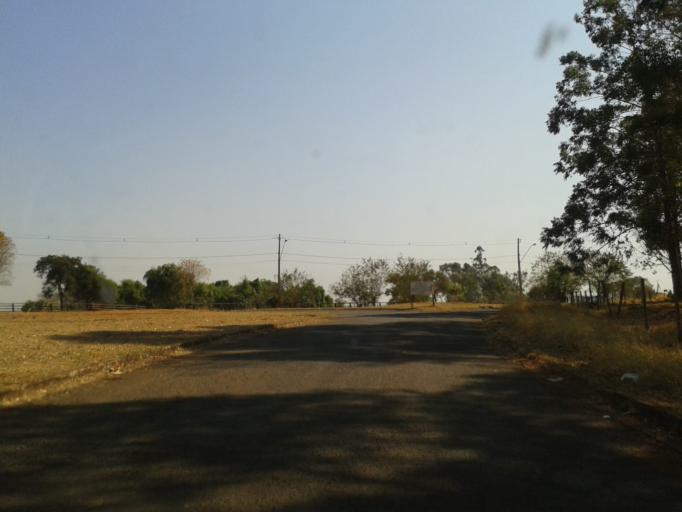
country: BR
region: Minas Gerais
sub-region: Ituiutaba
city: Ituiutaba
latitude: -18.9608
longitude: -49.4918
